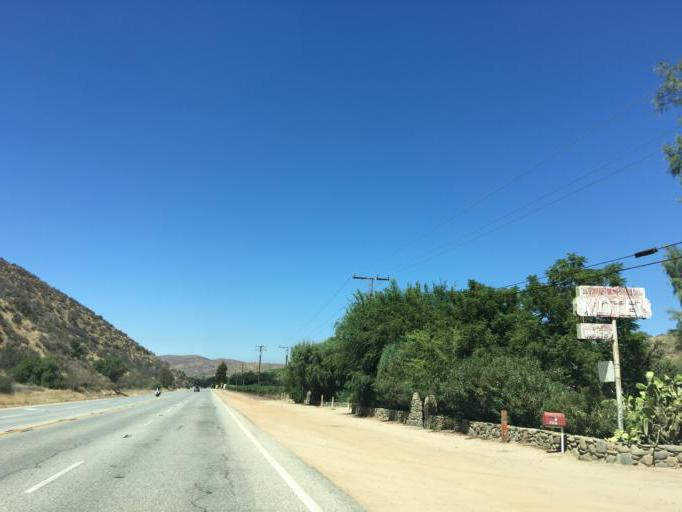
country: US
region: California
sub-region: Los Angeles County
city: Agua Dulce
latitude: 34.5115
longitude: -118.3470
